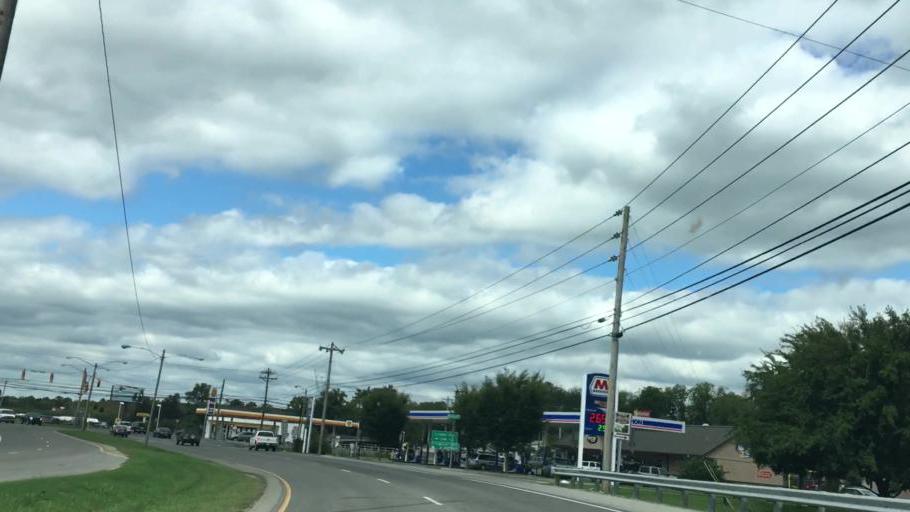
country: US
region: Tennessee
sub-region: Maury County
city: Columbia
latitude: 35.6164
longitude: -87.0649
